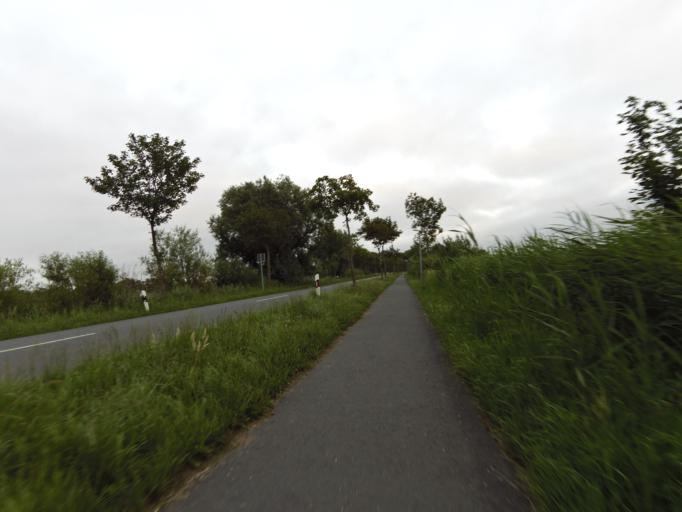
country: DE
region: Lower Saxony
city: Dorum
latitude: 53.7059
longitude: 8.5573
